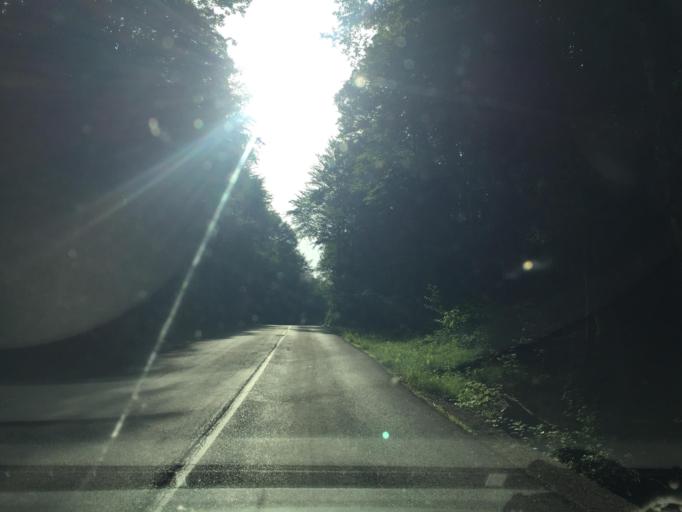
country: HR
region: Primorsko-Goranska
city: Matulji
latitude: 45.4184
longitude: 14.2299
